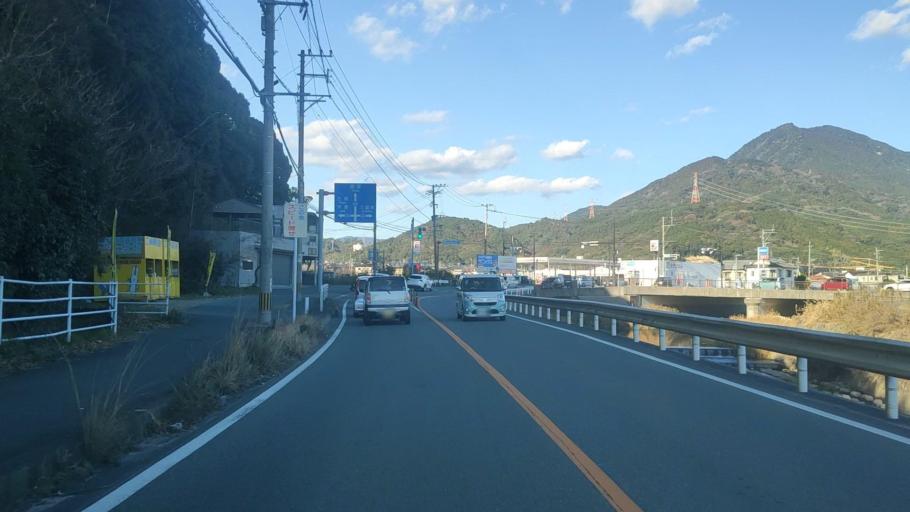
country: JP
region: Fukuoka
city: Dazaifu
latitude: 33.5050
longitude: 130.5512
